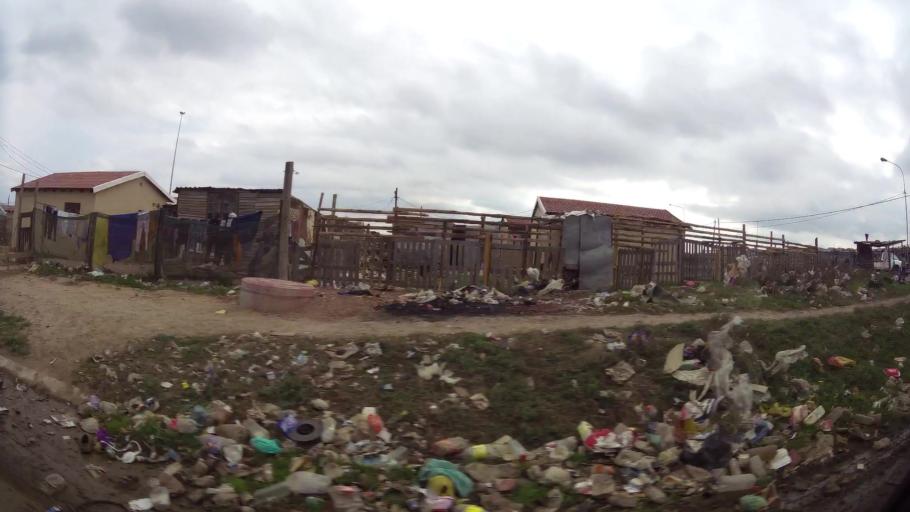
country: ZA
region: Eastern Cape
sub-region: Nelson Mandela Bay Metropolitan Municipality
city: Port Elizabeth
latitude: -33.8814
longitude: 25.5525
